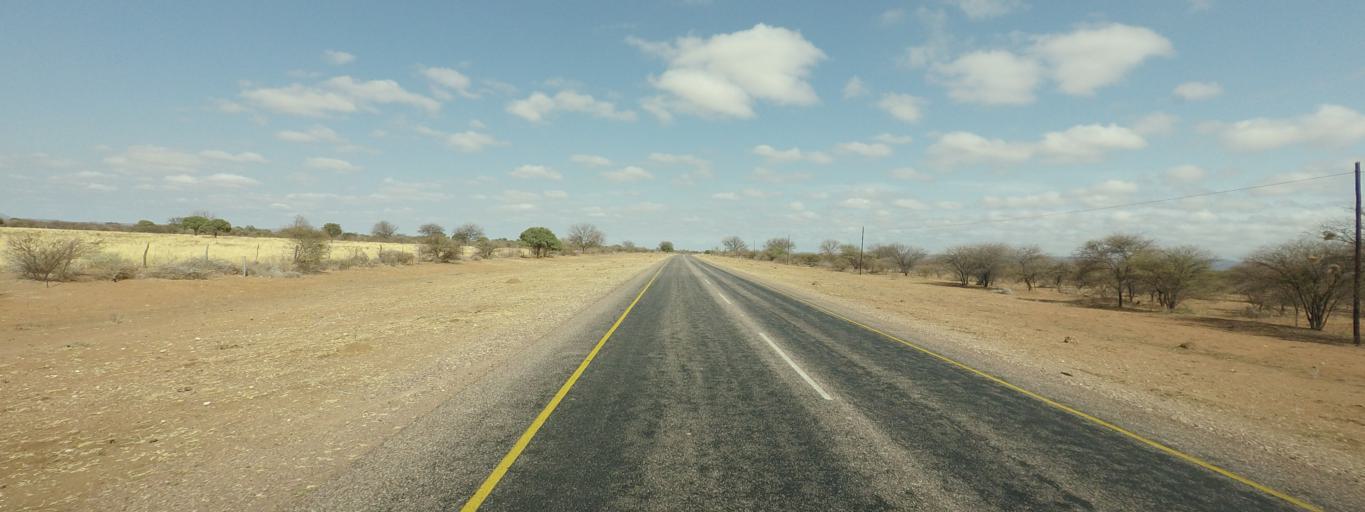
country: BW
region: Central
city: Ratholo
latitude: -22.8110
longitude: 27.5374
